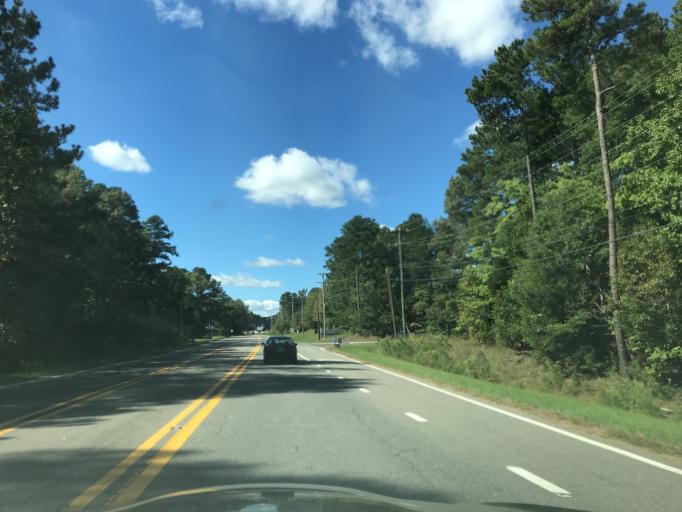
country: US
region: North Carolina
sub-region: Durham County
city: Gorman
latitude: 35.9767
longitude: -78.7795
